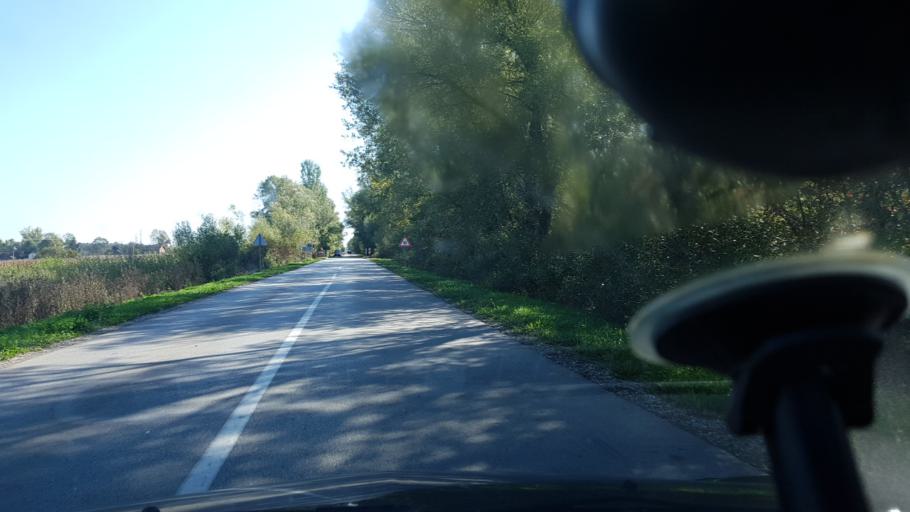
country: HR
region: Zagrebacka
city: Brckovljani
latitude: 45.7603
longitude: 16.2685
